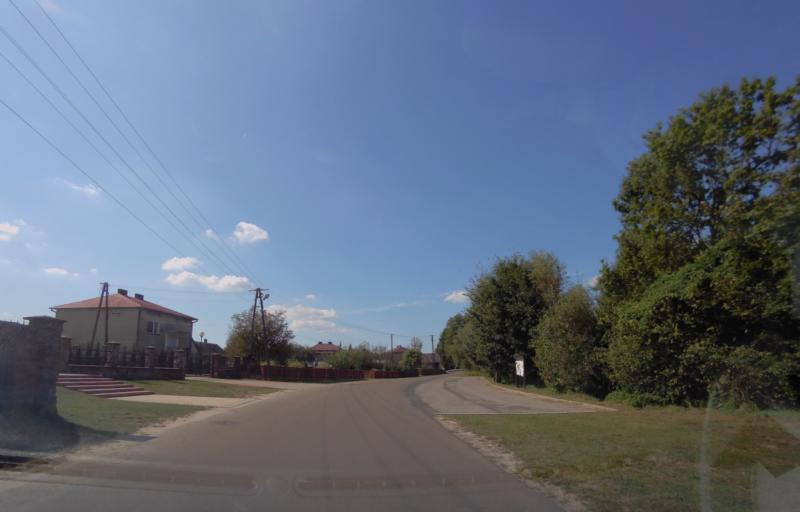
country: PL
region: Subcarpathian Voivodeship
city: Nowa Sarzyna
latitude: 50.3054
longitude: 22.3228
